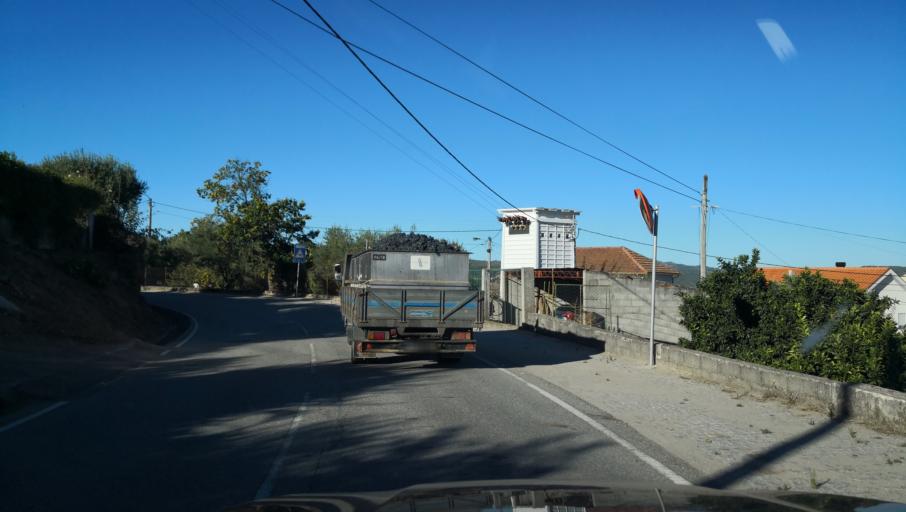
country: PT
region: Vila Real
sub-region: Sabrosa
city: Sabrosa
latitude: 41.2952
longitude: -7.5788
